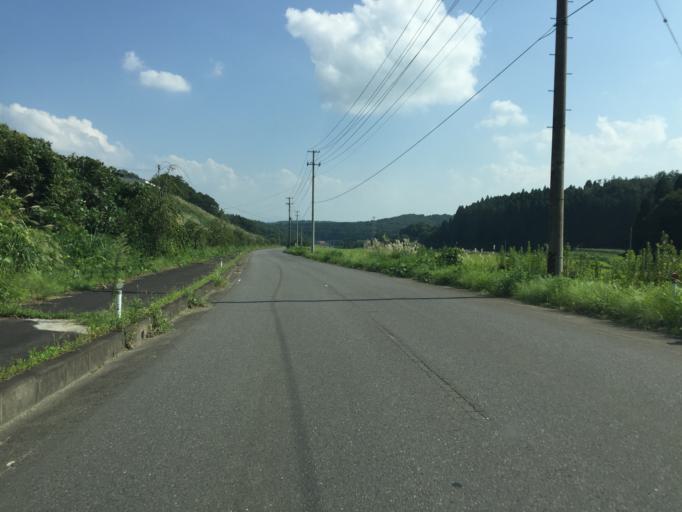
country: JP
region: Fukushima
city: Nihommatsu
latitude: 37.6064
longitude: 140.3962
